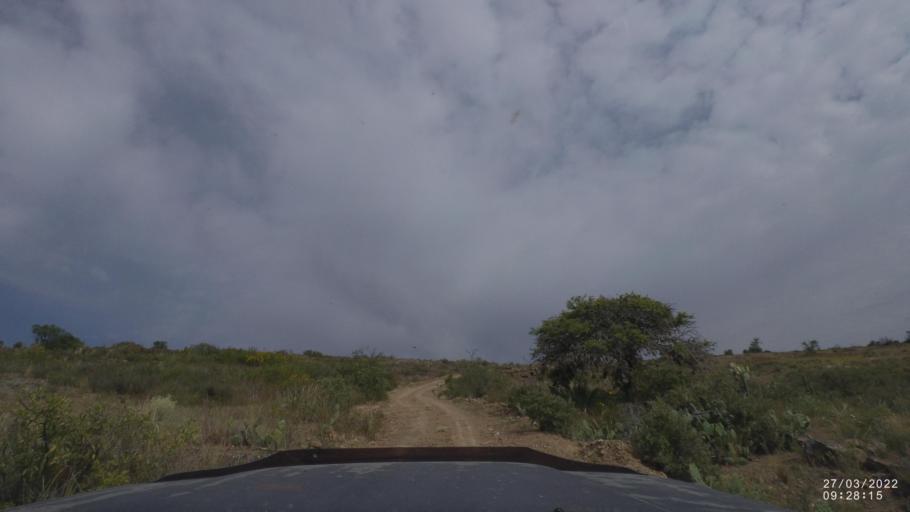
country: BO
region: Cochabamba
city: Cliza
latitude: -17.7303
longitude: -65.8777
